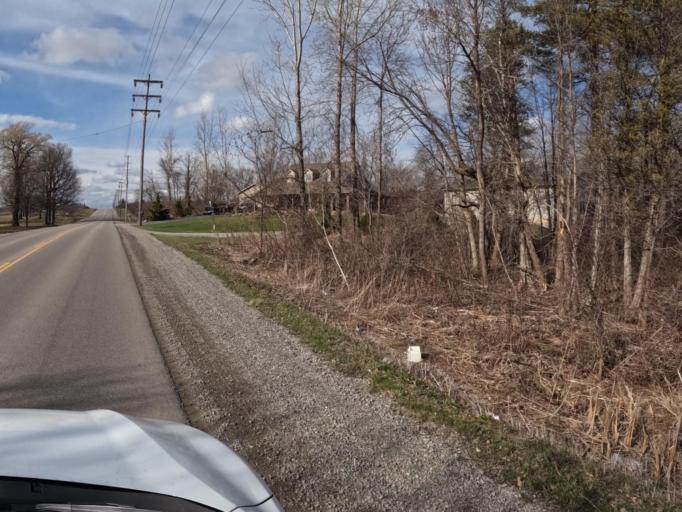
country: CA
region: Ontario
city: Norfolk County
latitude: 42.8570
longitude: -80.2649
